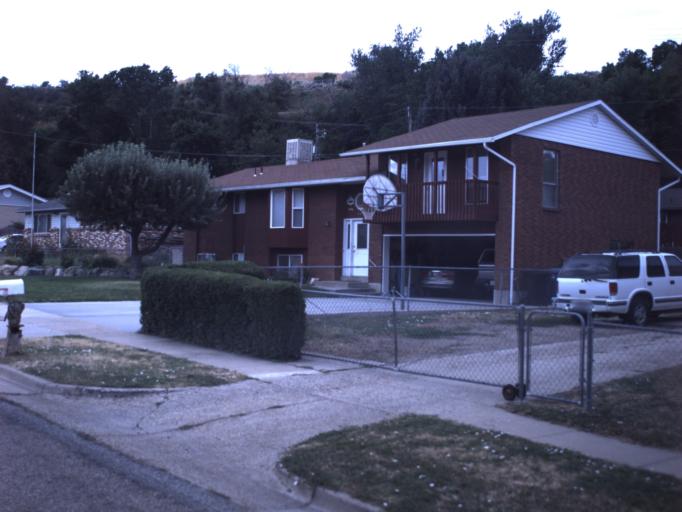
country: US
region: Utah
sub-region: Weber County
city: Riverdale
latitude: 41.1608
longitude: -112.0073
